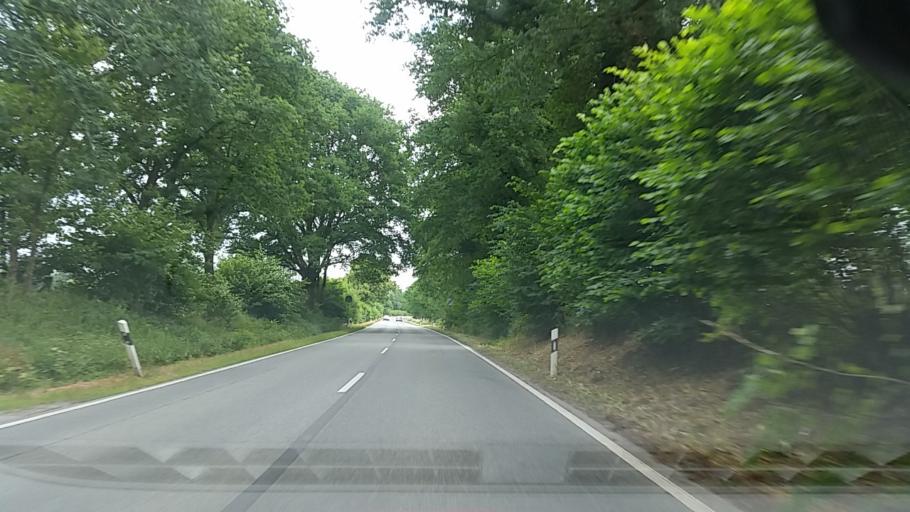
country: DE
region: Schleswig-Holstein
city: Sulfeld
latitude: 53.7669
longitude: 10.2283
